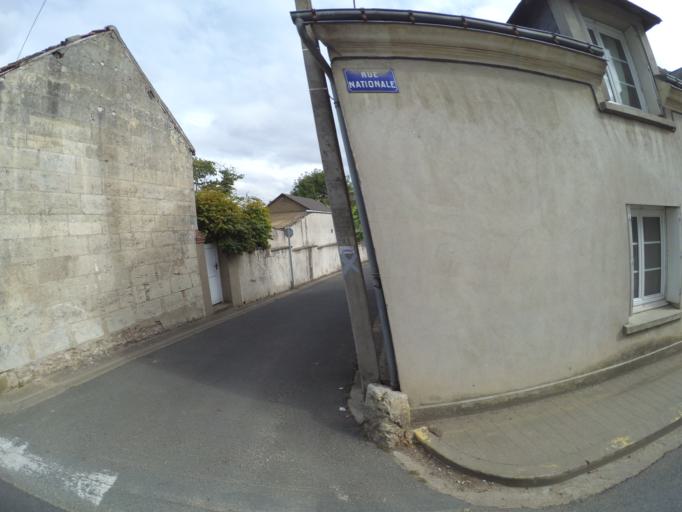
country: FR
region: Centre
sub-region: Departement d'Indre-et-Loire
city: Reugny
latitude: 47.4807
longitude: 0.8838
